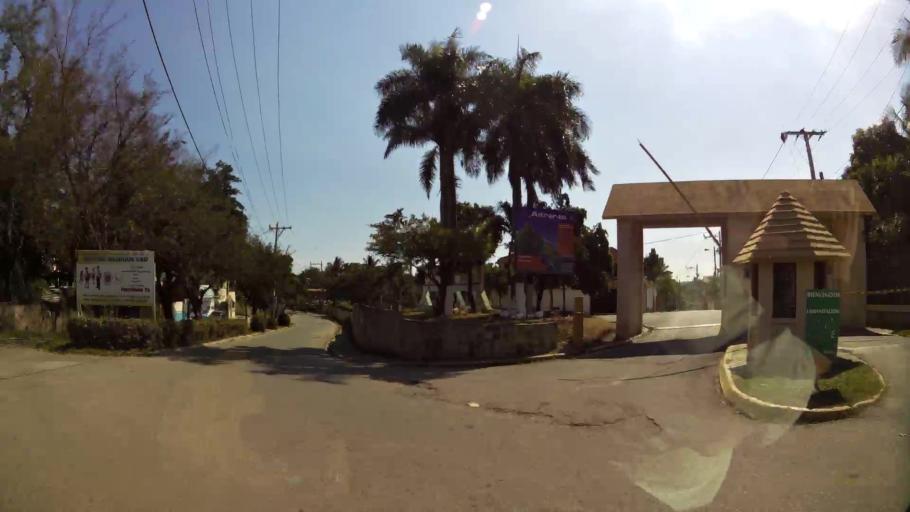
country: DO
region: Santo Domingo
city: Santo Domingo Oeste
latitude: 18.4752
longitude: -70.0002
